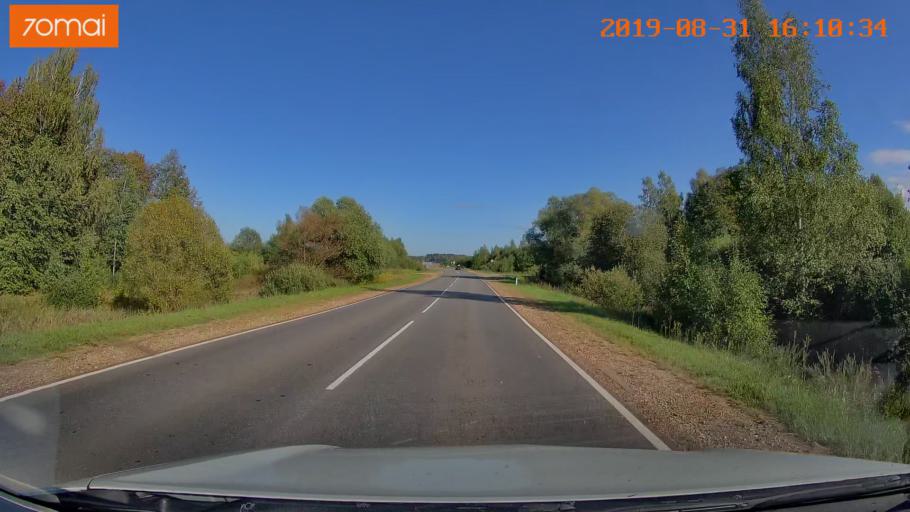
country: RU
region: Kaluga
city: Nikola-Lenivets
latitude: 54.5831
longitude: 35.4281
